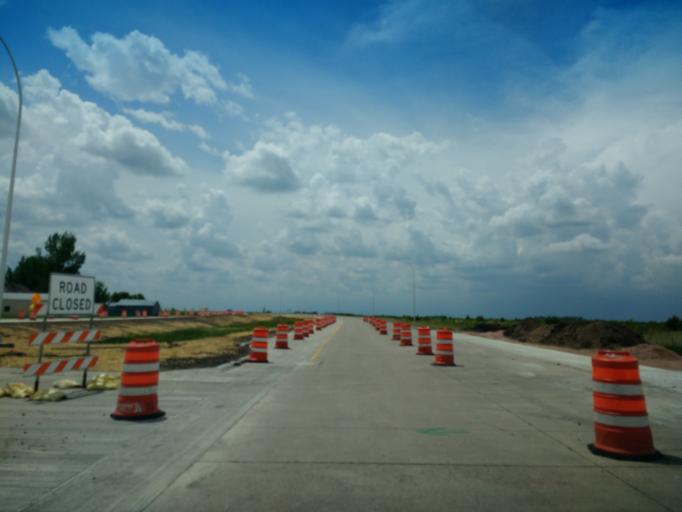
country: US
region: Minnesota
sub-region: Jackson County
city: Lakefield
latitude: 43.7984
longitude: -95.3245
